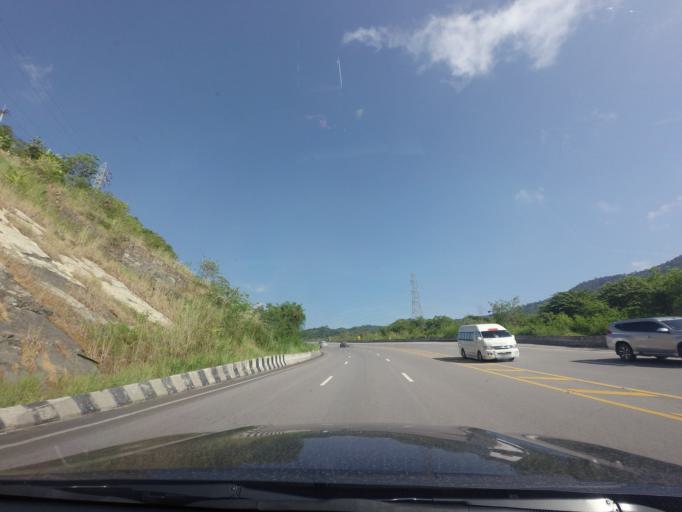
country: TH
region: Phetchabun
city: Lom Sak
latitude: 16.7777
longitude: 101.1183
